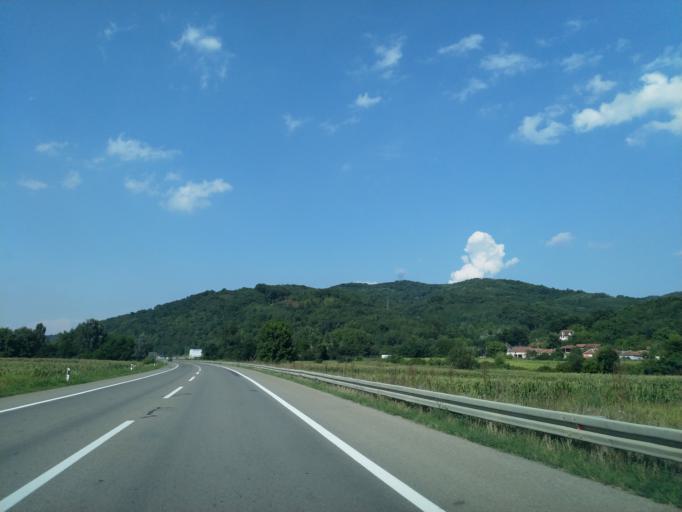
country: RS
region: Central Serbia
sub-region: Rasinski Okrug
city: Krusevac
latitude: 43.6220
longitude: 21.3721
